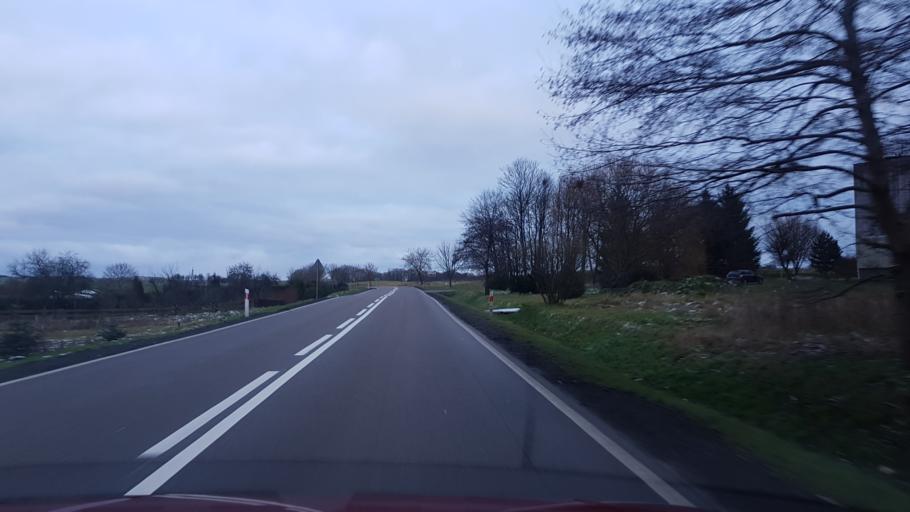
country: PL
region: Pomeranian Voivodeship
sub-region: Powiat czluchowski
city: Koczala
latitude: 54.0243
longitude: 17.1761
